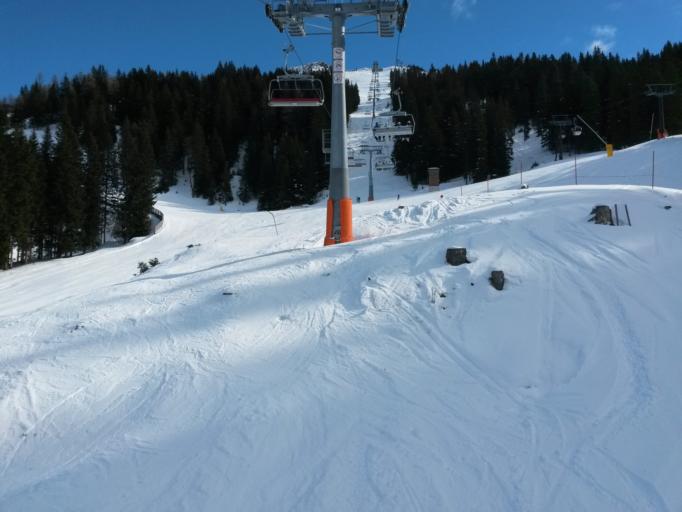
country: AT
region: Salzburg
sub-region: Politischer Bezirk Sankt Johann im Pongau
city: Dorfgastein
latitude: 47.2390
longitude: 13.1361
